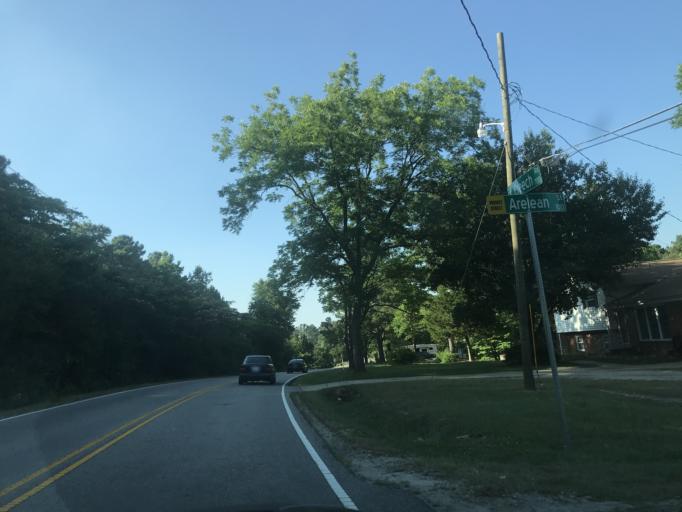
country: US
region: North Carolina
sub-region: Wake County
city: Garner
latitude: 35.7176
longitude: -78.6024
